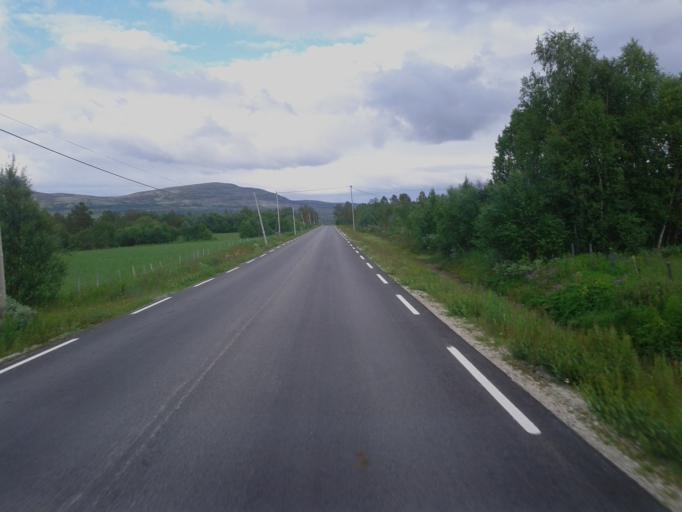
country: NO
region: Sor-Trondelag
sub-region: Roros
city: Roros
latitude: 62.3063
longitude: 11.6976
